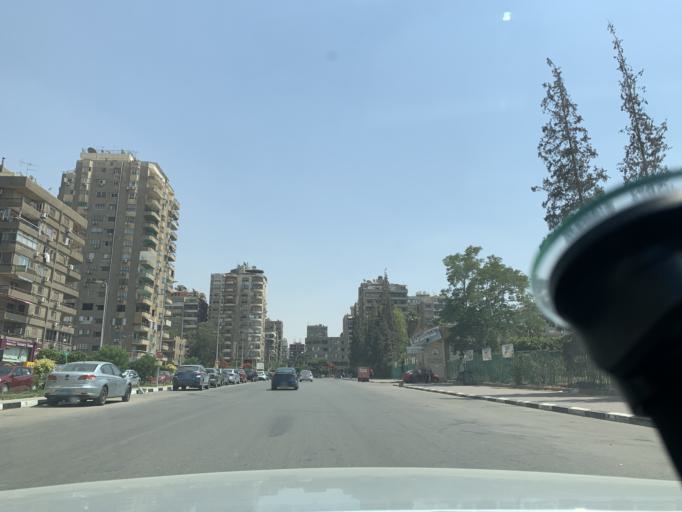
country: EG
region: Muhafazat al Qahirah
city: Cairo
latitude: 30.0627
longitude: 31.3494
